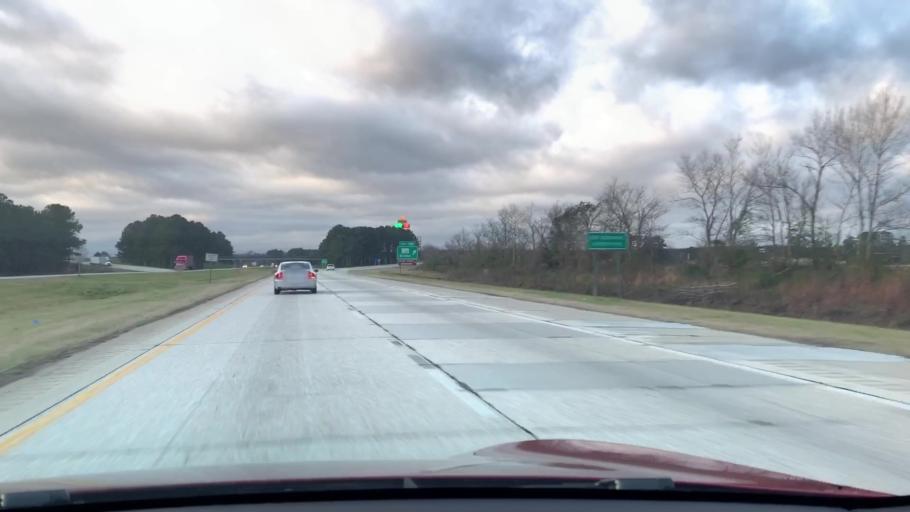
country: US
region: South Carolina
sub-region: Dillon County
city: Dillon
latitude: 34.4225
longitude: -79.4094
